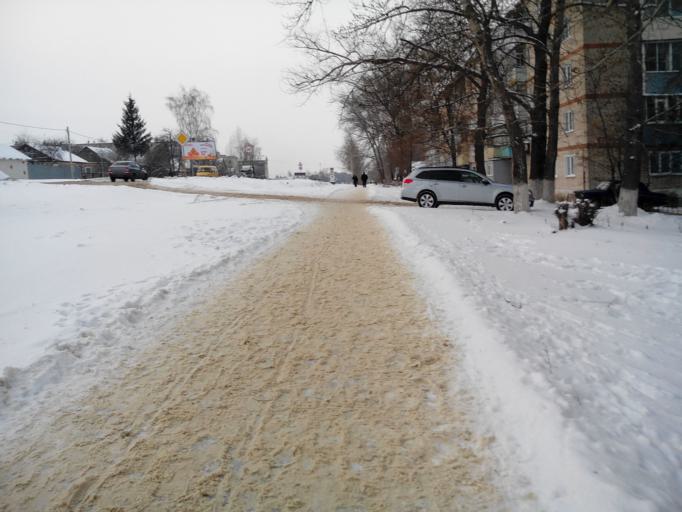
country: RU
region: Tula
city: Yefremov
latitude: 53.1485
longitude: 38.0831
